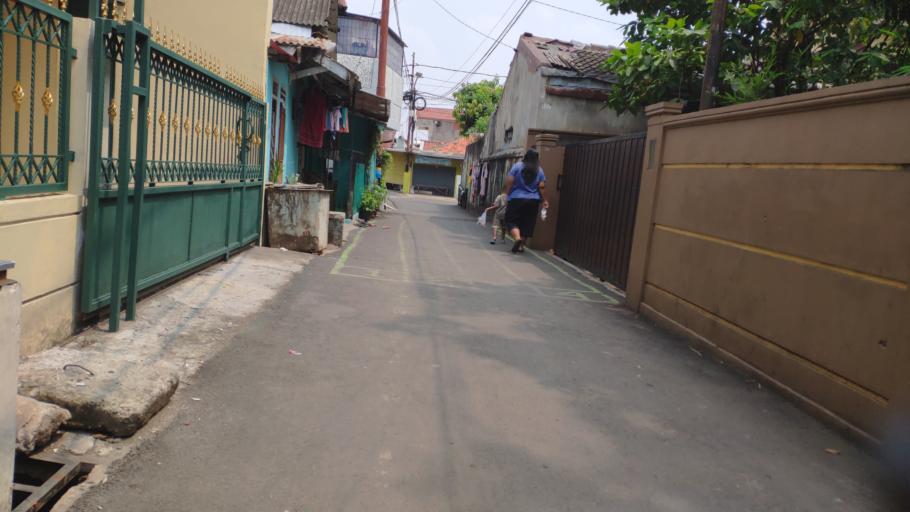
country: ID
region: West Java
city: Pamulang
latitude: -6.3042
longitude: 106.8184
